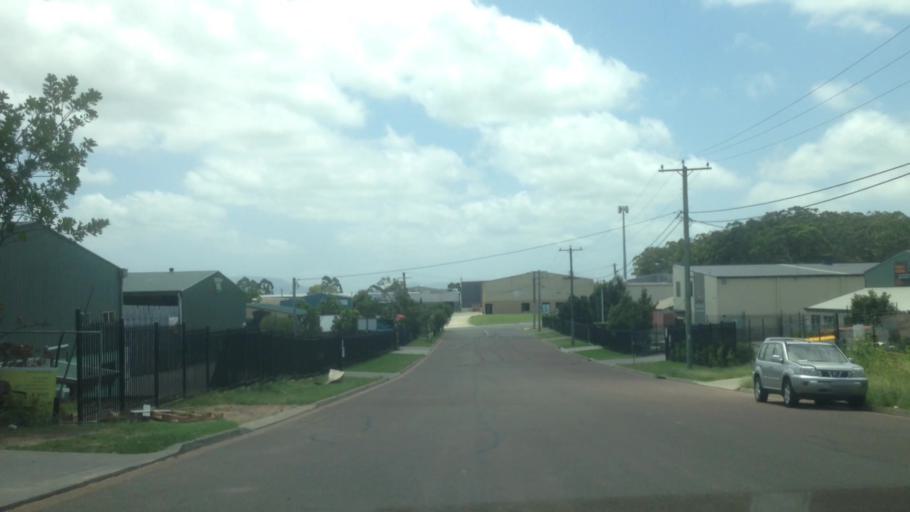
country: AU
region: New South Wales
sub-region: Lake Macquarie Shire
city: Dora Creek
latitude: -33.1195
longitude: 151.4732
